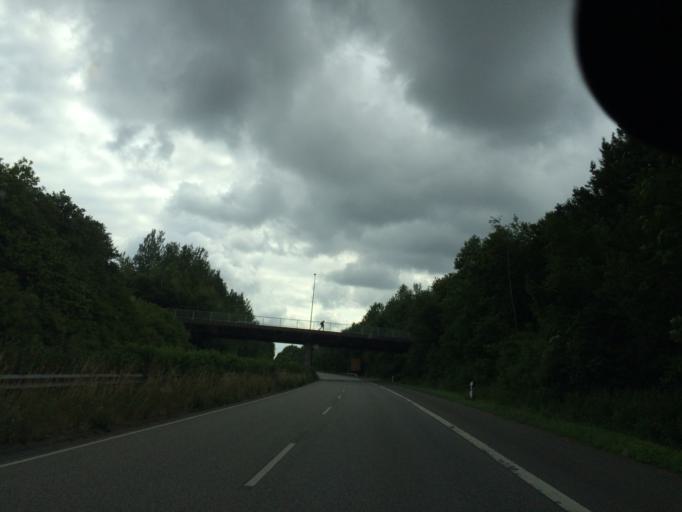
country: DE
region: Schleswig-Holstein
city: Kronshagen
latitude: 54.3529
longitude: 10.1028
